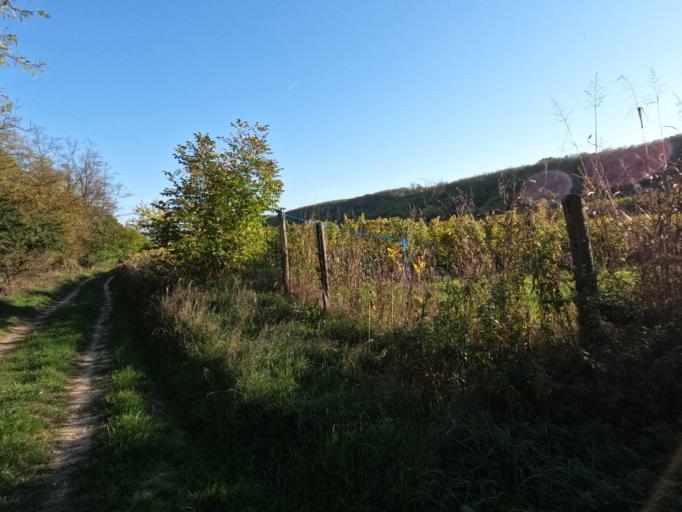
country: HU
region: Tolna
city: Szekszard
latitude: 46.3043
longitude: 18.6575
